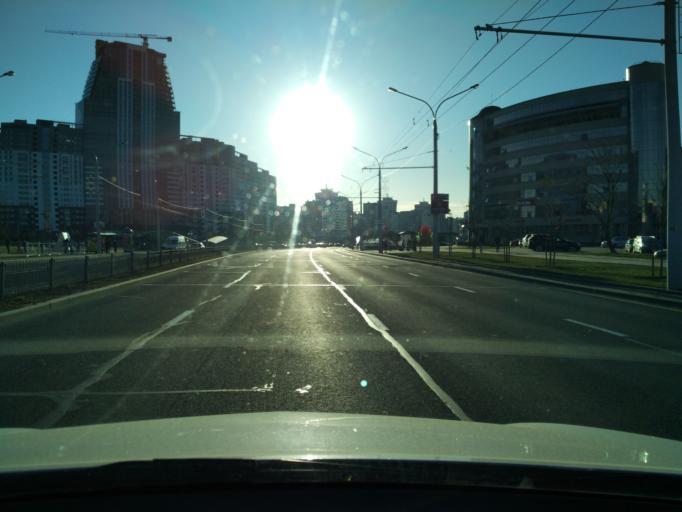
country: BY
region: Minsk
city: Zhdanovichy
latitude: 53.9375
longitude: 27.4836
